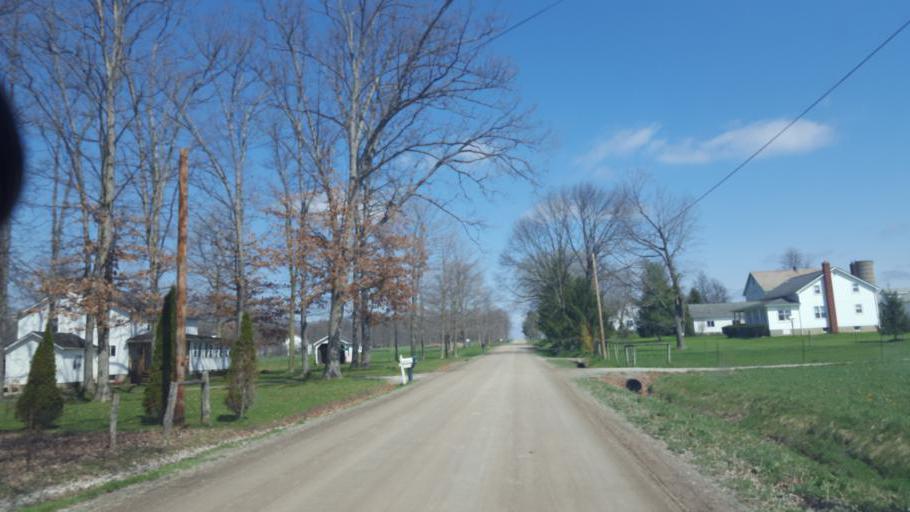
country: US
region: Ohio
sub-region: Geauga County
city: Middlefield
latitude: 41.3955
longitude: -81.0801
